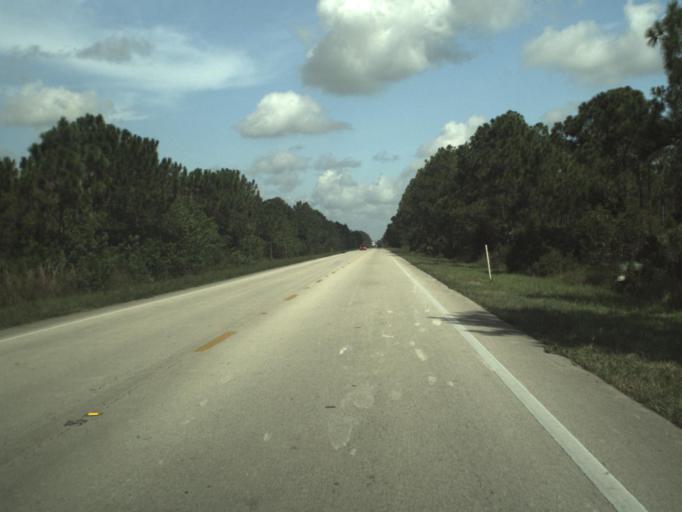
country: US
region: Florida
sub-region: Martin County
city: Indiantown
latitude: 26.9730
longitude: -80.3964
